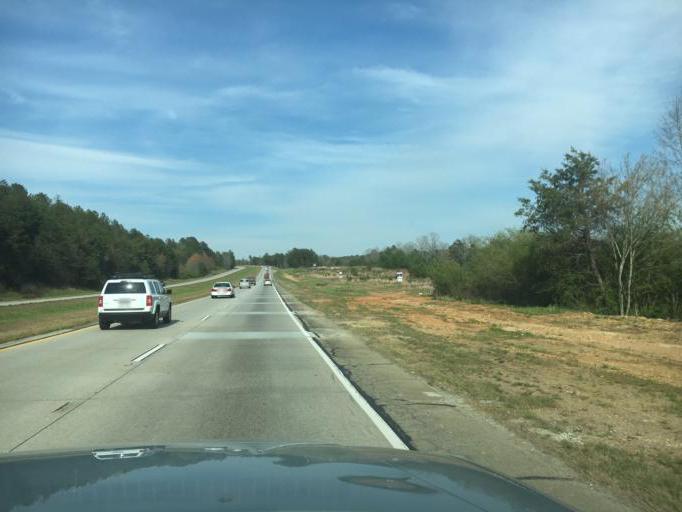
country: US
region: Georgia
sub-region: Hall County
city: Lula
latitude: 34.3761
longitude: -83.7211
